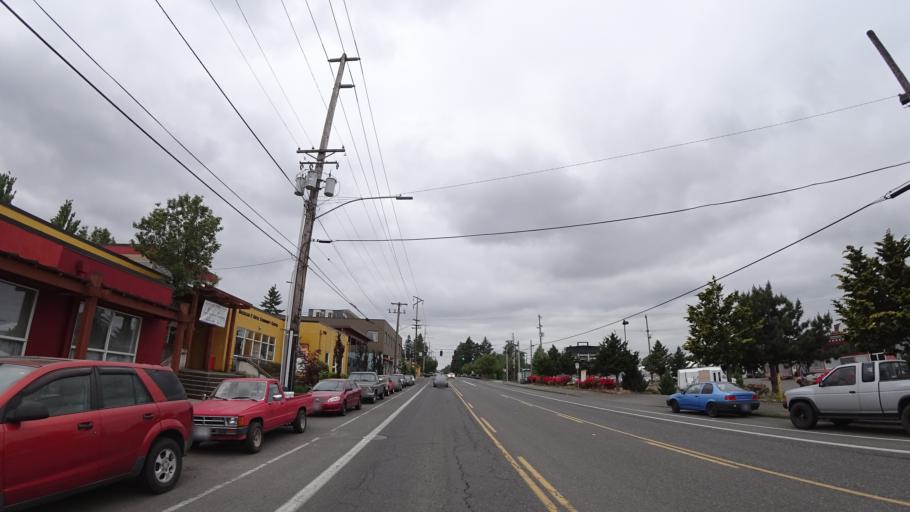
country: US
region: Oregon
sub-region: Multnomah County
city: Lents
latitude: 45.5627
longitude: -122.5930
